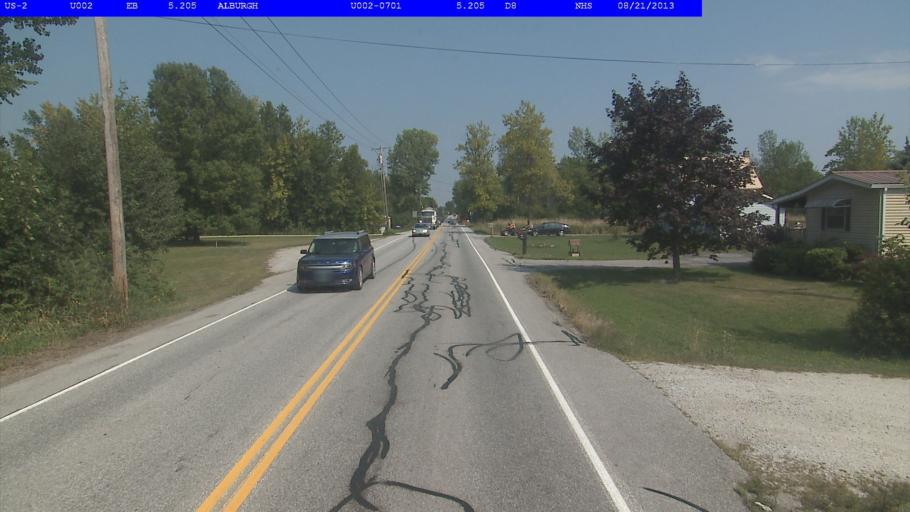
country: US
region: New York
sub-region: Clinton County
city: Rouses Point
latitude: 44.9653
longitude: -73.2944
